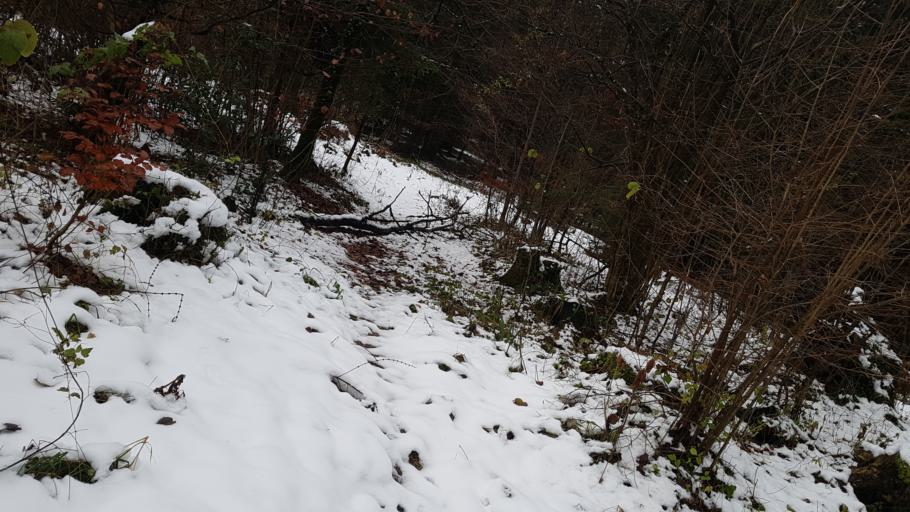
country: AT
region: Salzburg
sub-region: Politischer Bezirk Salzburg-Umgebung
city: Grodig
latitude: 47.7257
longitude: 13.0366
